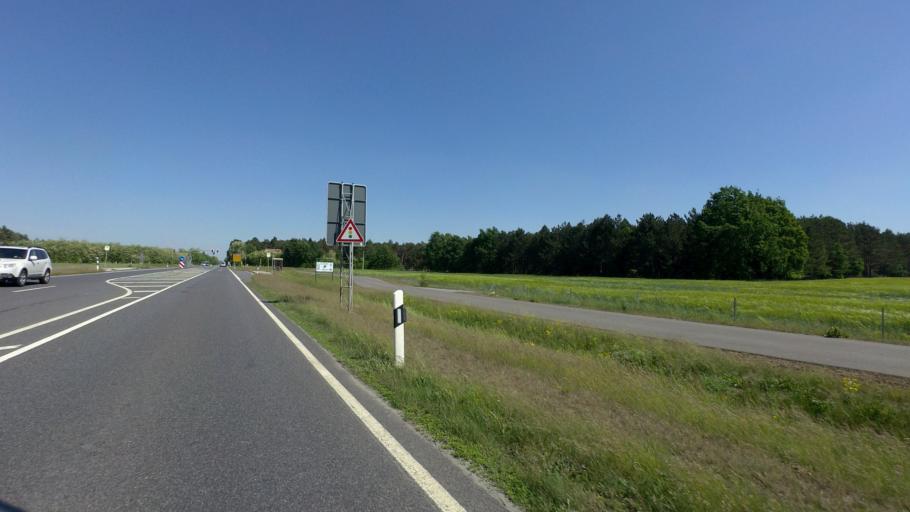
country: DE
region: Brandenburg
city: Spremberg
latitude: 51.6097
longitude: 14.3634
